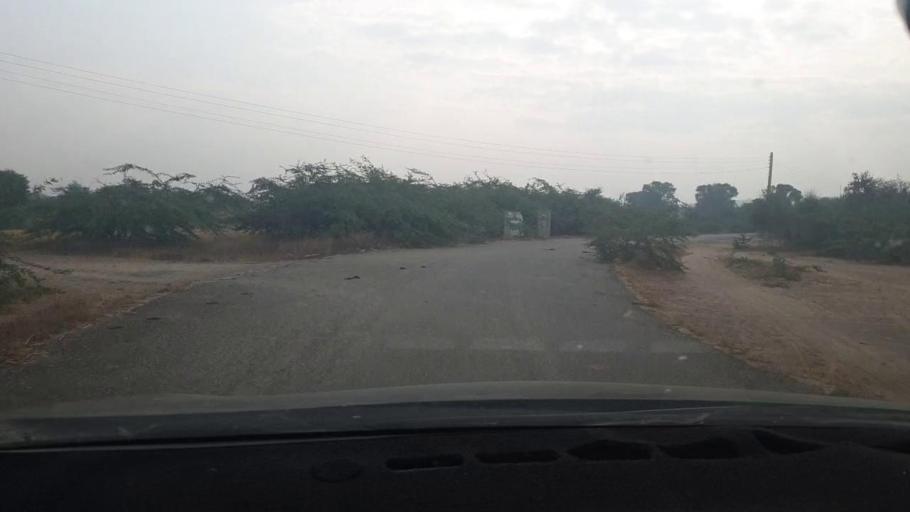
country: PK
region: Sindh
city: Malir Cantonment
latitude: 24.9557
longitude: 67.4097
